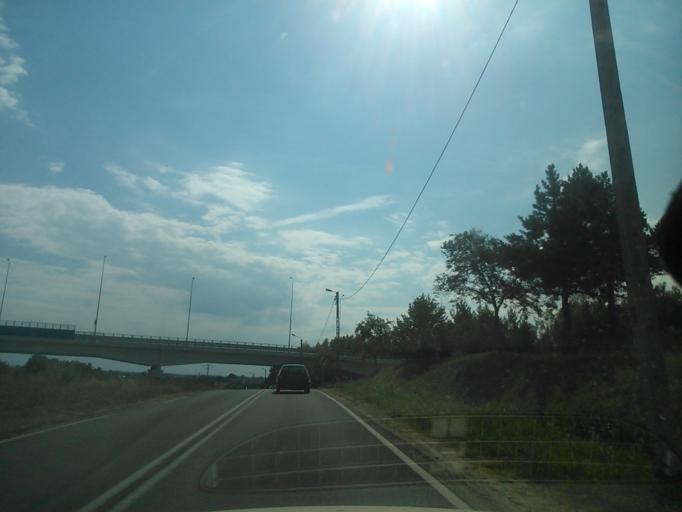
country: PL
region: Warmian-Masurian Voivodeship
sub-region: Powiat dzialdowski
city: Ilowo -Osada
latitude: 53.1427
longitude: 20.3393
